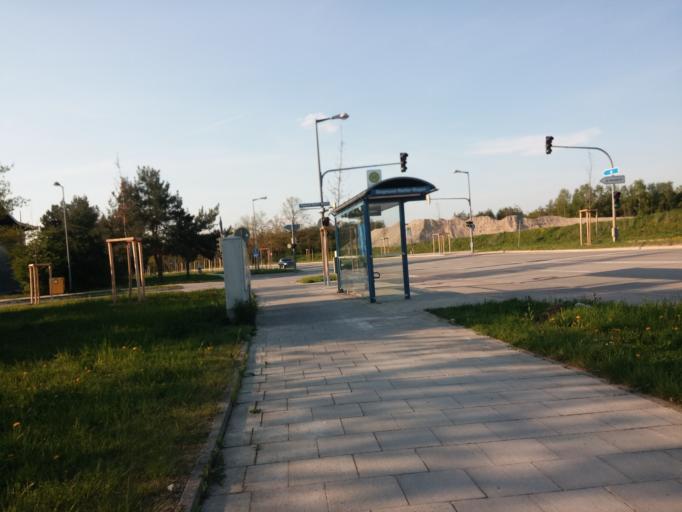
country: DE
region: Bavaria
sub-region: Upper Bavaria
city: Feldkirchen
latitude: 48.1363
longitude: 11.7152
